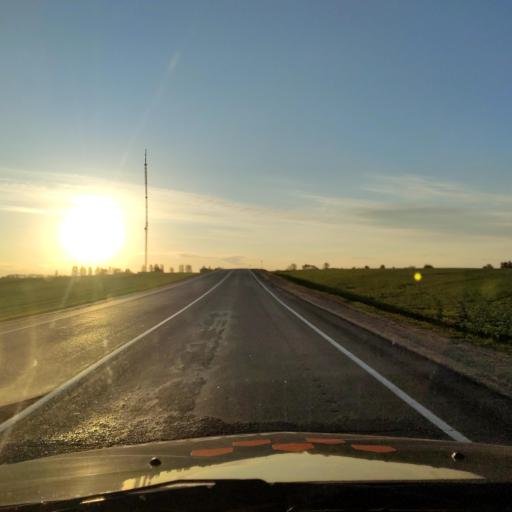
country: RU
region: Orjol
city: Livny
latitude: 52.4491
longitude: 37.4882
